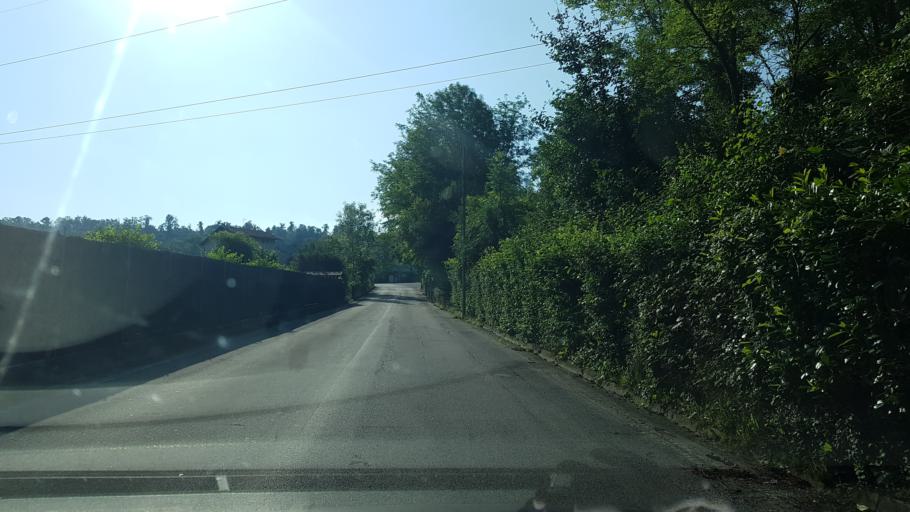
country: IT
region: Veneto
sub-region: Provincia di Belluno
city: Belluno
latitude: 46.1266
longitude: 12.2120
